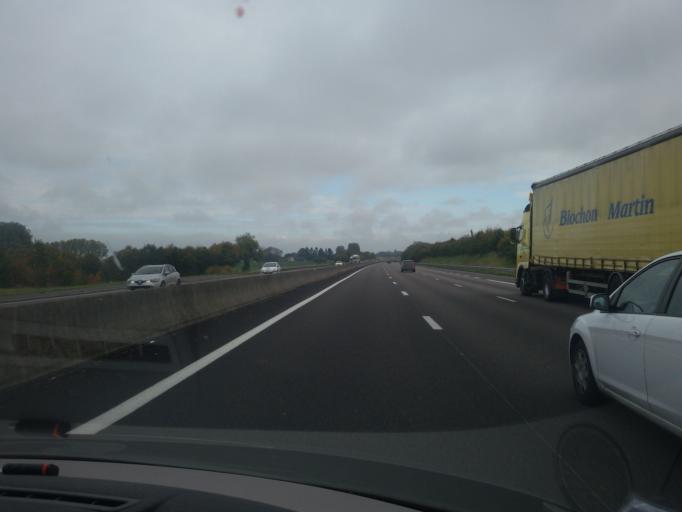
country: FR
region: Haute-Normandie
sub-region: Departement de l'Eure
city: Hauville
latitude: 49.3718
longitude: 0.6910
